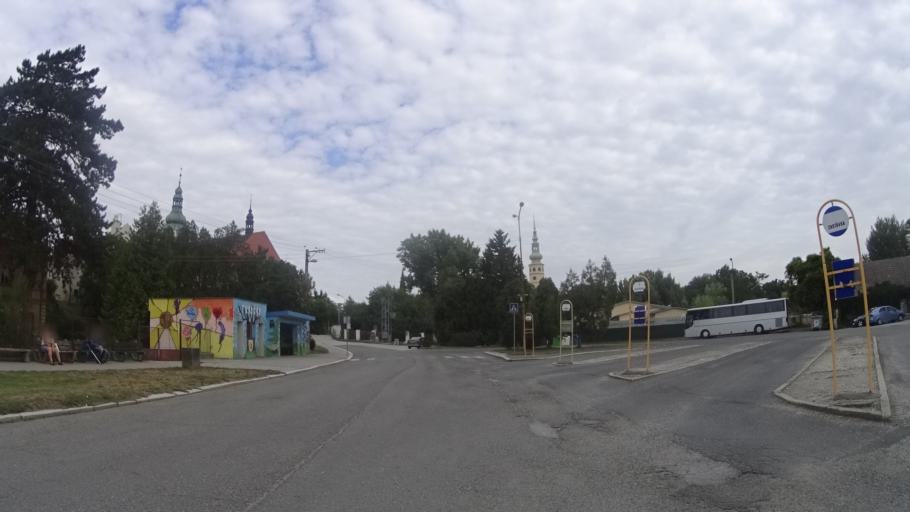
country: CZ
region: Olomoucky
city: Tovacov
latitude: 49.4267
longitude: 17.2912
